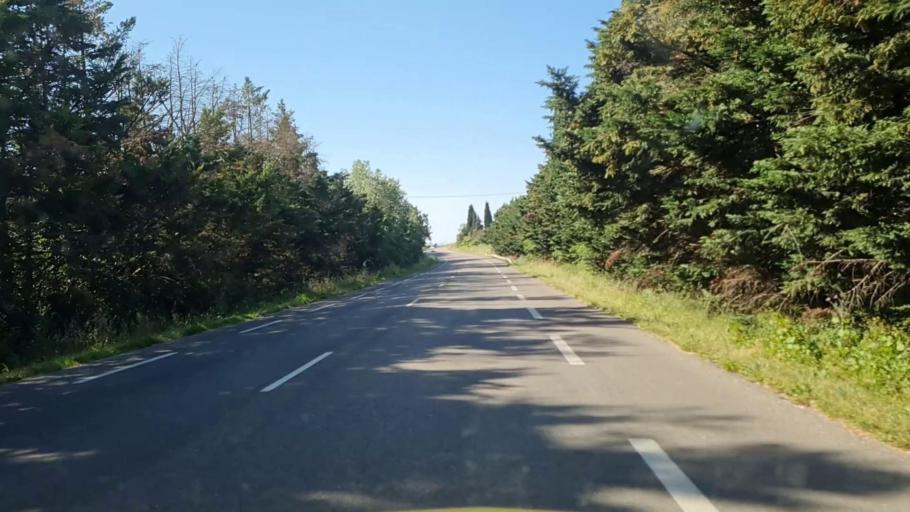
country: FR
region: Languedoc-Roussillon
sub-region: Departement du Gard
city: Garons
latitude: 43.7355
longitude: 4.4099
